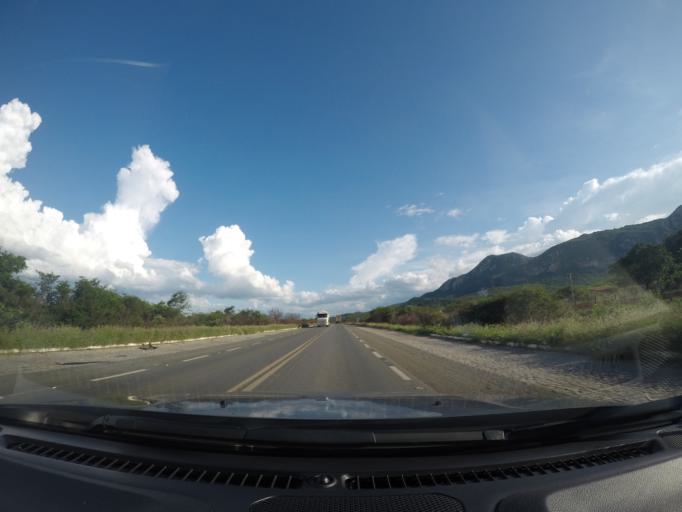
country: BR
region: Bahia
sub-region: Oliveira Dos Brejinhos
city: Oliveira dos Brejinhos
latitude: -12.0576
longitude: -42.9640
